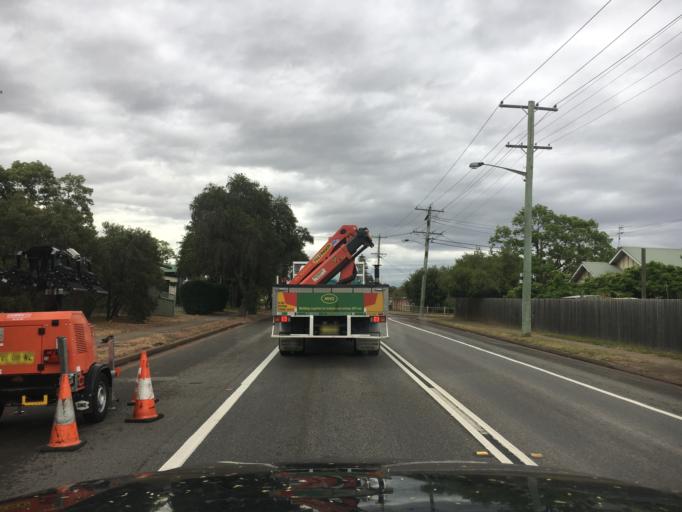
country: AU
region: New South Wales
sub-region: Singleton
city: Singleton
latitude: -32.5671
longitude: 151.1787
